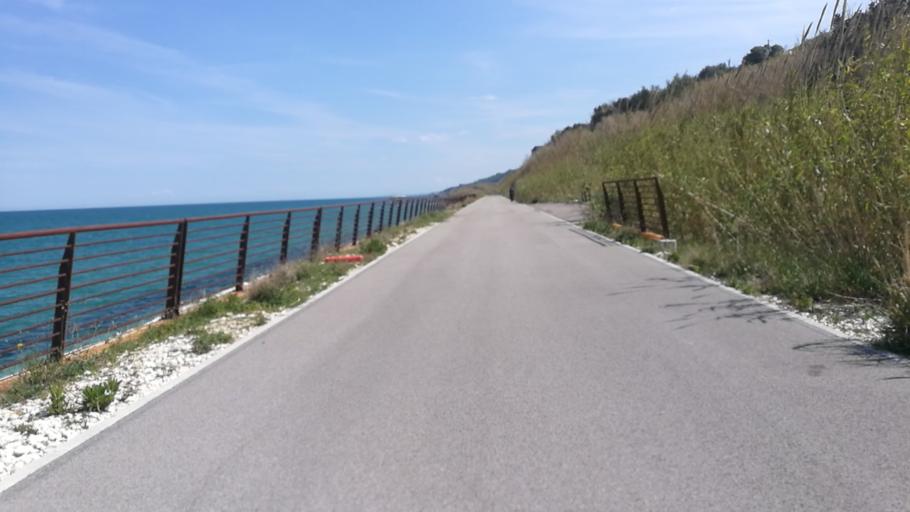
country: IT
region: Abruzzo
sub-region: Provincia di Chieti
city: Marina di San Vito
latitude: 42.3212
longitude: 14.4313
